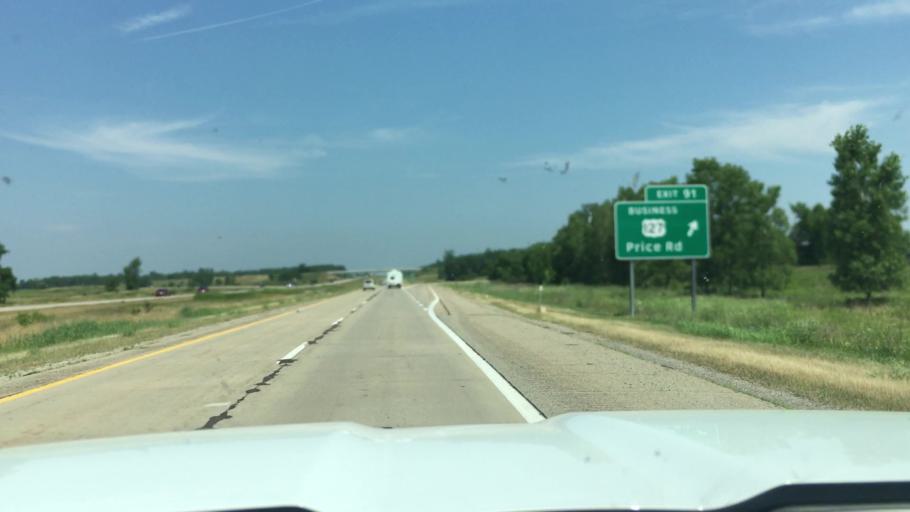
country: US
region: Michigan
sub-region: Clinton County
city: Saint Johns
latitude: 42.9201
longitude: -84.5186
